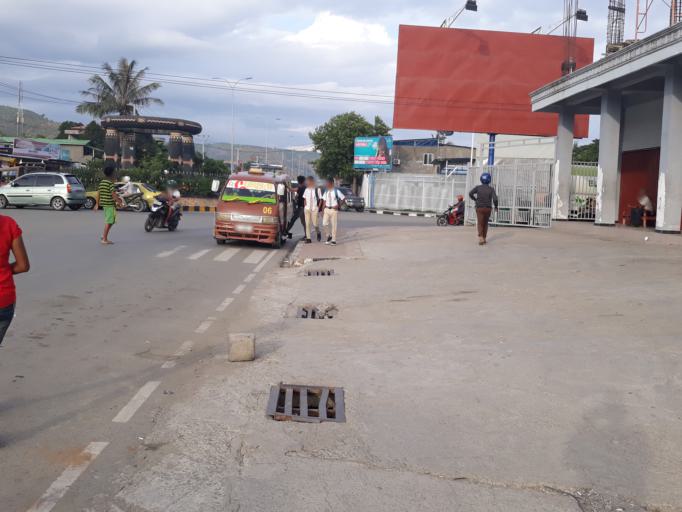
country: TL
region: Dili
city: Dili
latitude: -8.5606
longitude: 125.5415
